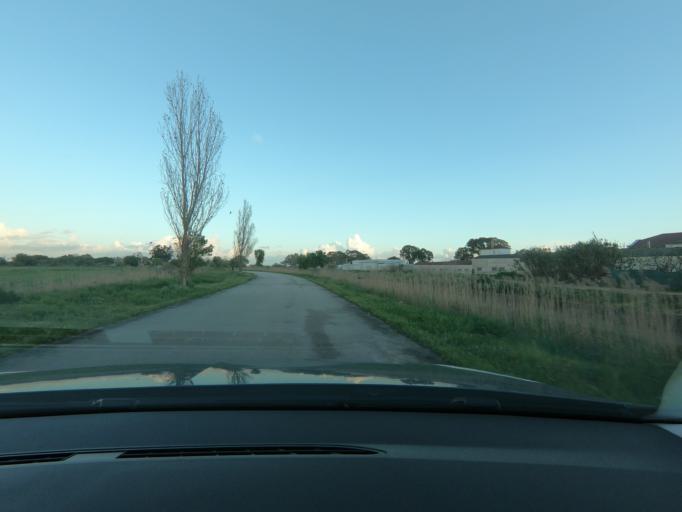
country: PT
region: Lisbon
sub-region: Vila Franca de Xira
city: Castanheira do Ribatejo
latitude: 39.0050
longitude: -8.9483
